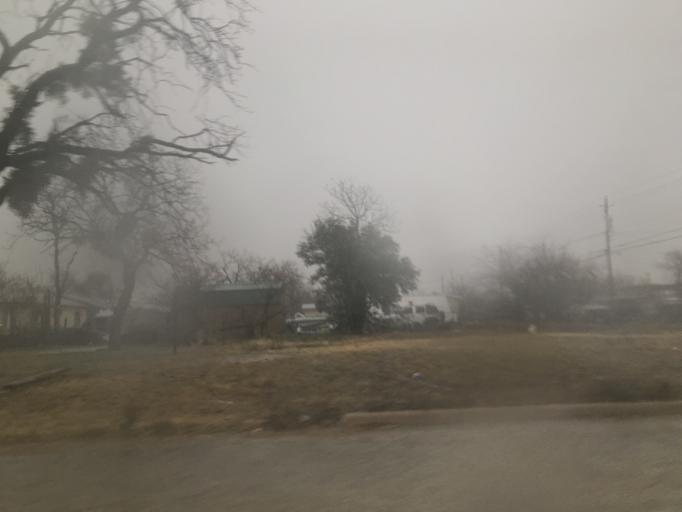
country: US
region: Texas
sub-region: Tom Green County
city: San Angelo
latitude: 31.4662
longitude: -100.4175
